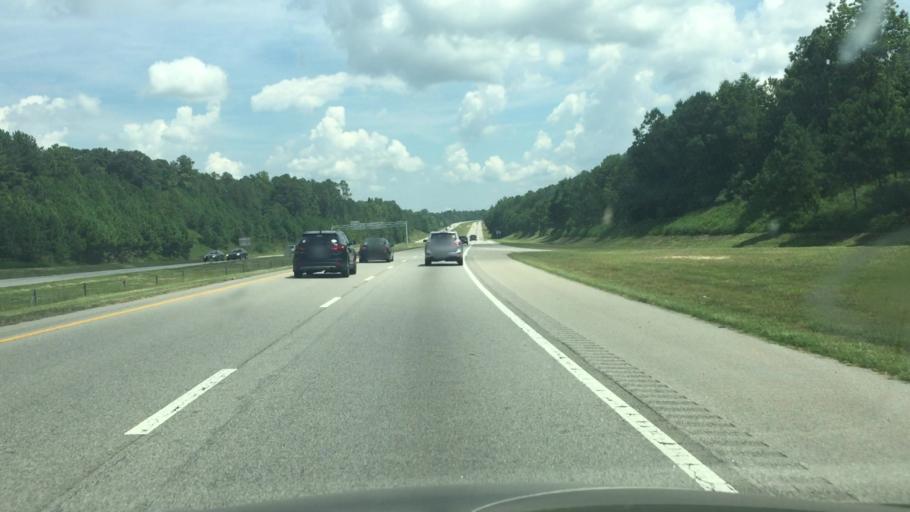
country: US
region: North Carolina
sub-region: Richmond County
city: Ellerbe
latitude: 35.0452
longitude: -79.7662
